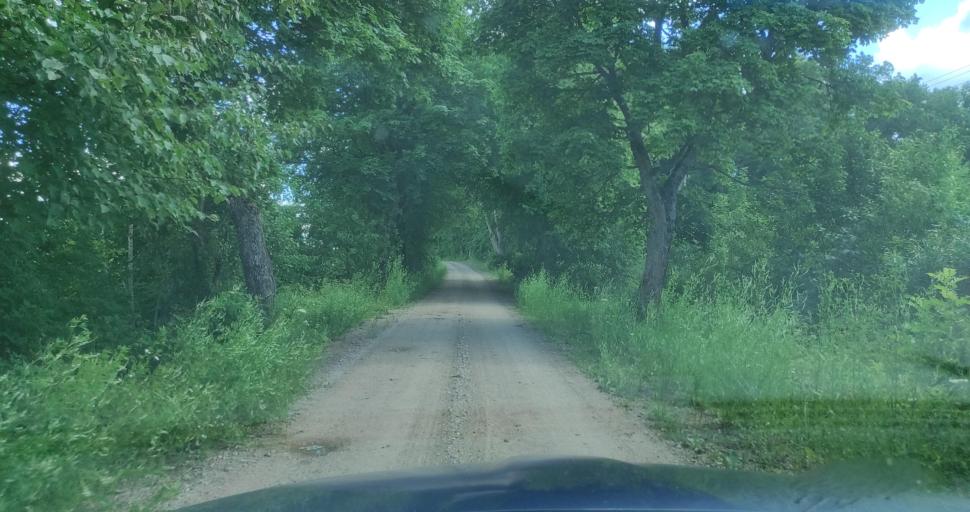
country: LV
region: Kuldigas Rajons
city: Kuldiga
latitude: 57.0014
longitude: 22.1500
